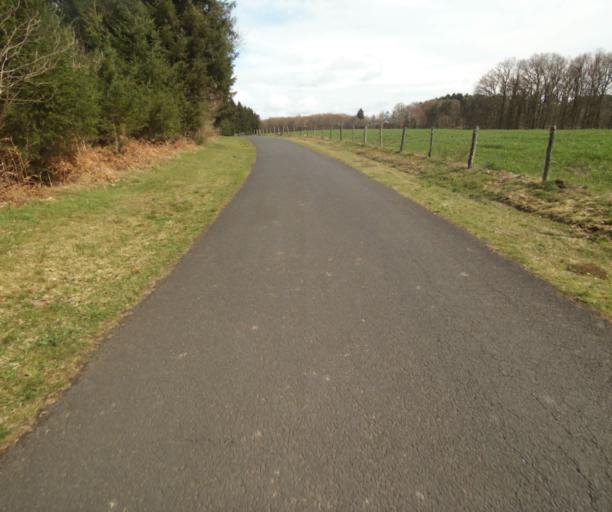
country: FR
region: Limousin
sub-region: Departement de la Correze
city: Correze
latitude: 45.3527
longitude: 1.8975
